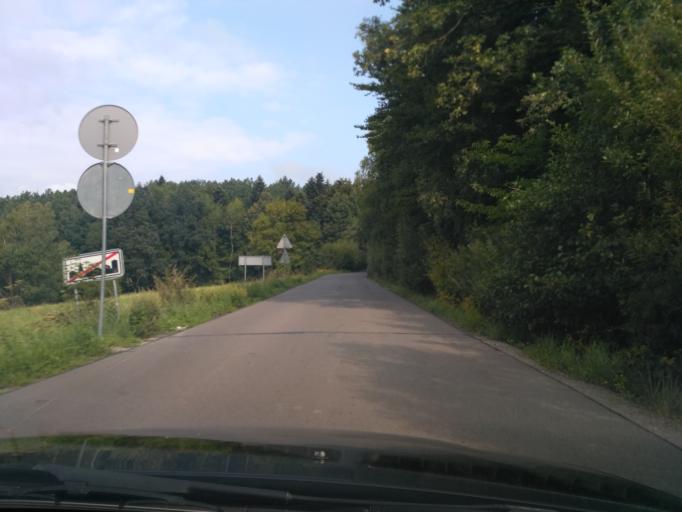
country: PL
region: Subcarpathian Voivodeship
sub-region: Powiat strzyzowski
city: Czudec
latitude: 49.9638
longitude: 21.8424
